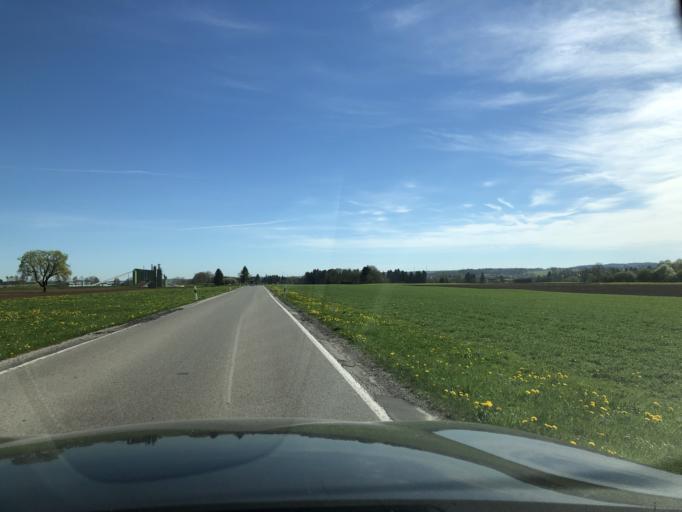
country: DE
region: Bavaria
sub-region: Swabia
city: Marktoberdorf
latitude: 47.7619
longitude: 10.5741
